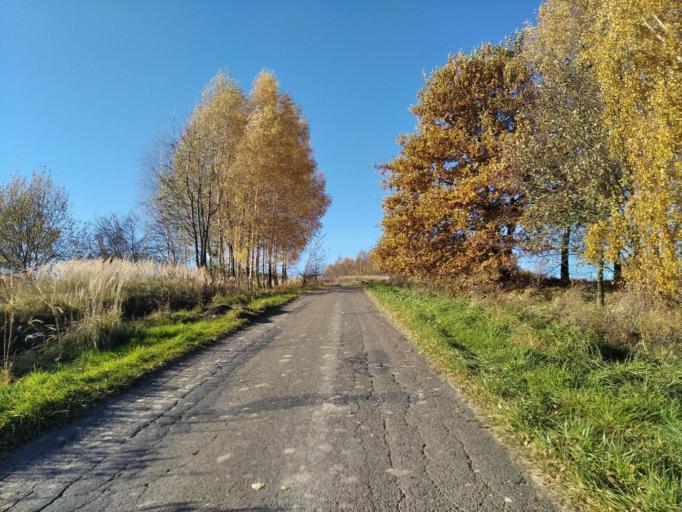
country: PL
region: Subcarpathian Voivodeship
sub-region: Powiat strzyzowski
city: Frysztak
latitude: 49.8617
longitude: 21.6174
